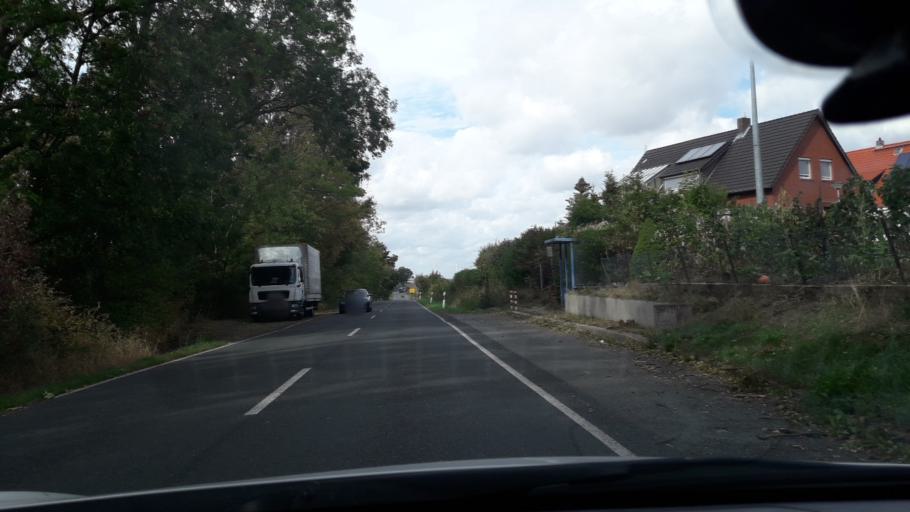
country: DE
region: Lower Saxony
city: Alt Wallmoden
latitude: 52.0247
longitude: 10.3484
